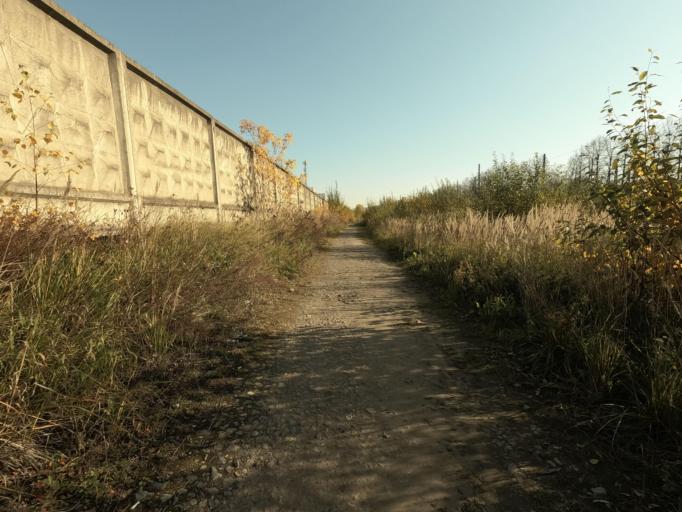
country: RU
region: St.-Petersburg
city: Obukhovo
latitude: 59.8436
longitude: 30.4693
